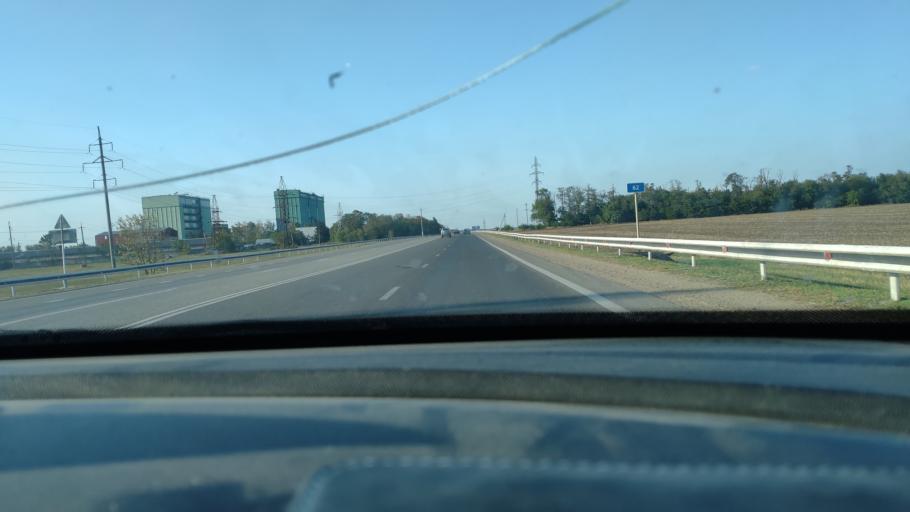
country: RU
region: Krasnodarskiy
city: Timashevsk
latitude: 45.6146
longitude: 38.9872
